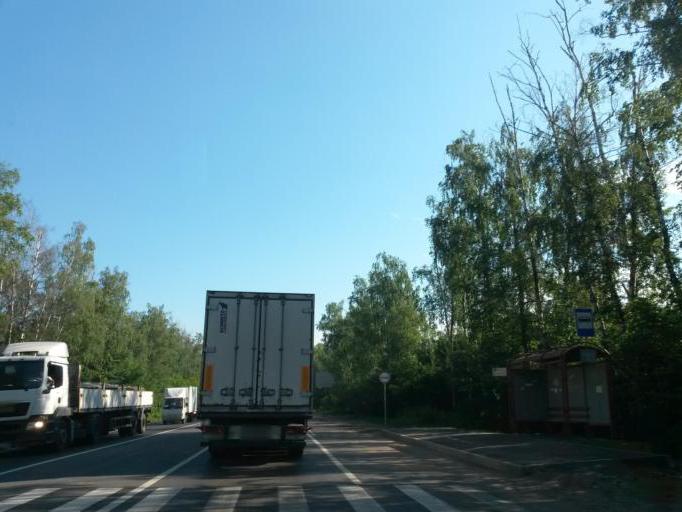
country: RU
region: Moskovskaya
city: Petrovskaya
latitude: 55.5376
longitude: 37.7702
